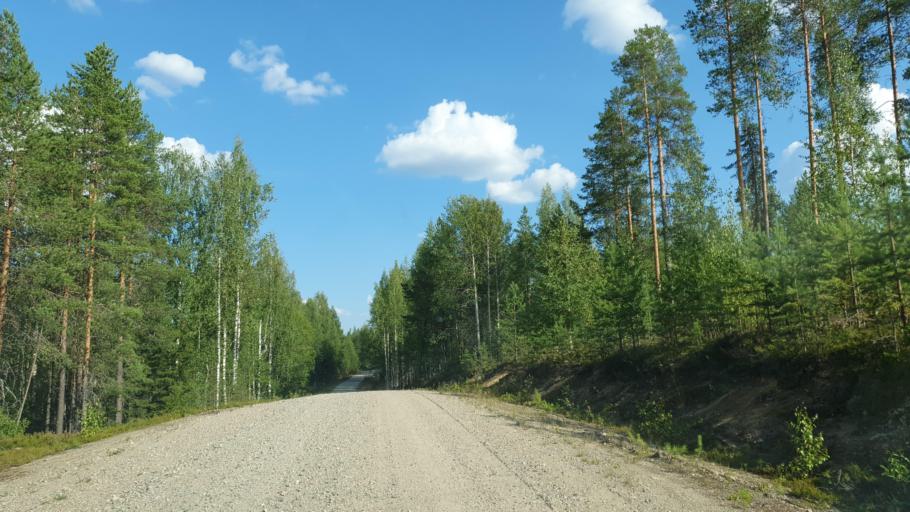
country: FI
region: Kainuu
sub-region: Kehys-Kainuu
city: Kuhmo
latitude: 63.9532
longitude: 29.5597
